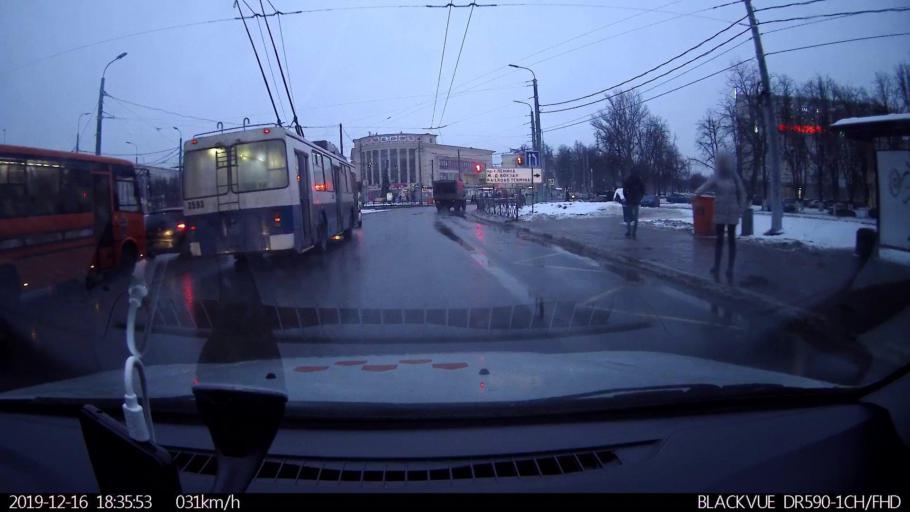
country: RU
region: Nizjnij Novgorod
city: Gorbatovka
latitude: 56.2418
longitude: 43.8640
